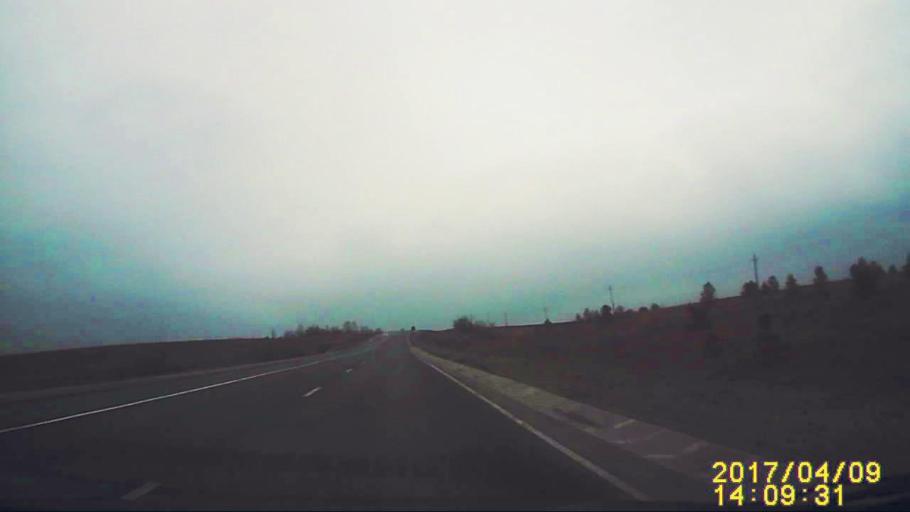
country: RU
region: Ulyanovsk
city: Krasnyy Gulyay
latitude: 54.0295
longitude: 48.2130
